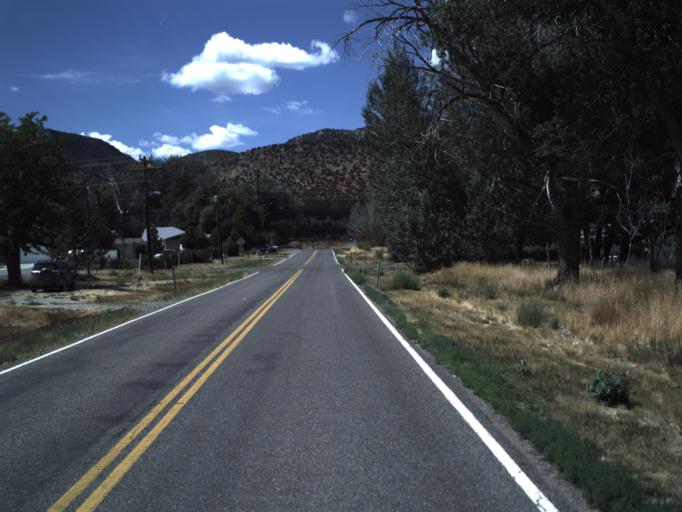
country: US
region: Utah
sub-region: Sanpete County
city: Moroni
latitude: 39.4884
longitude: -111.6361
